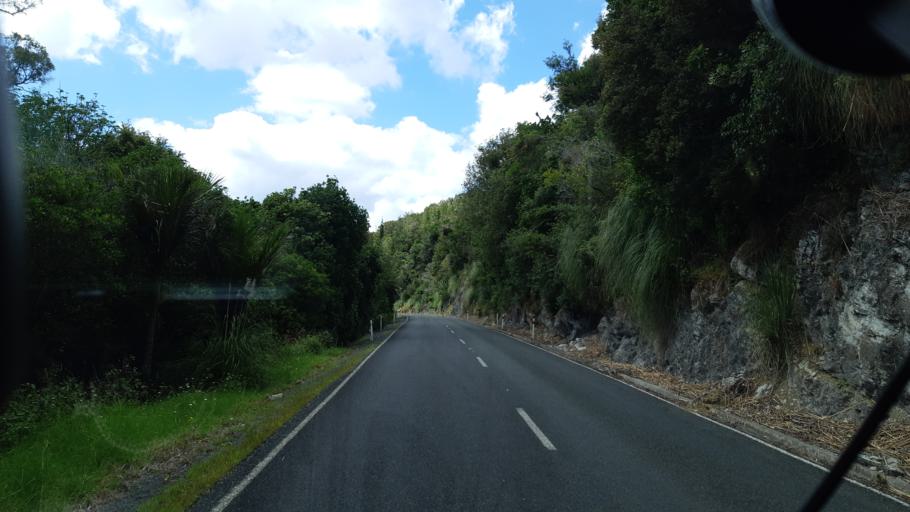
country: NZ
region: Northland
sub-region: Far North District
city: Taipa
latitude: -35.2513
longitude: 173.5321
